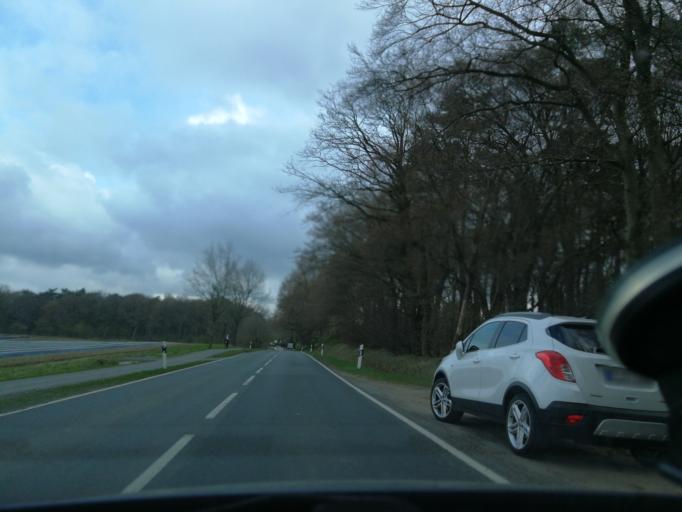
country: DE
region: Lower Saxony
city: Seevetal
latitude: 53.4385
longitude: 9.9154
